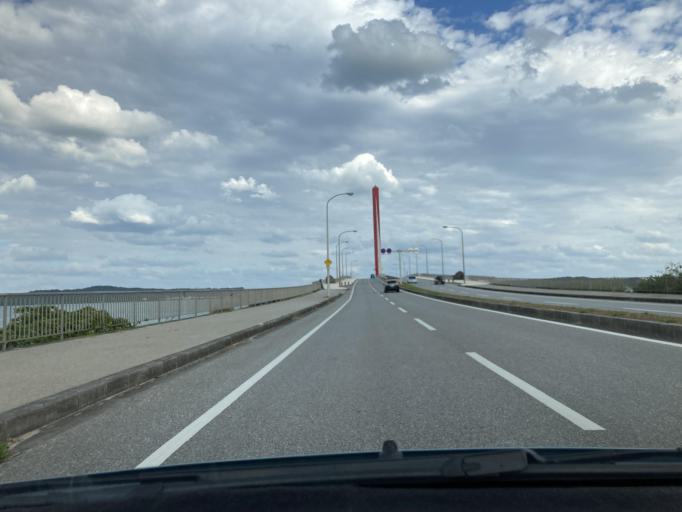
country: JP
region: Okinawa
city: Katsuren-haebaru
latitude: 26.3318
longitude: 127.9135
